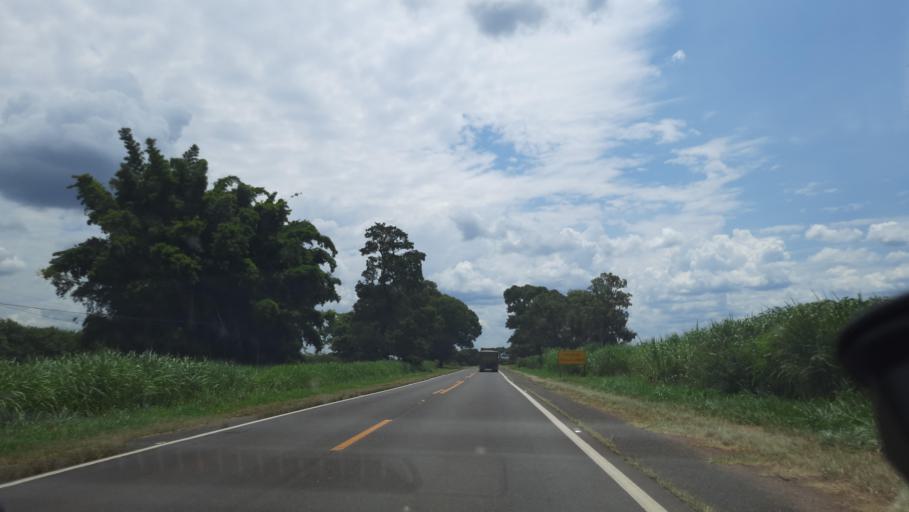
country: BR
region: Sao Paulo
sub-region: Mococa
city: Mococa
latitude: -21.5140
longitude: -47.0373
